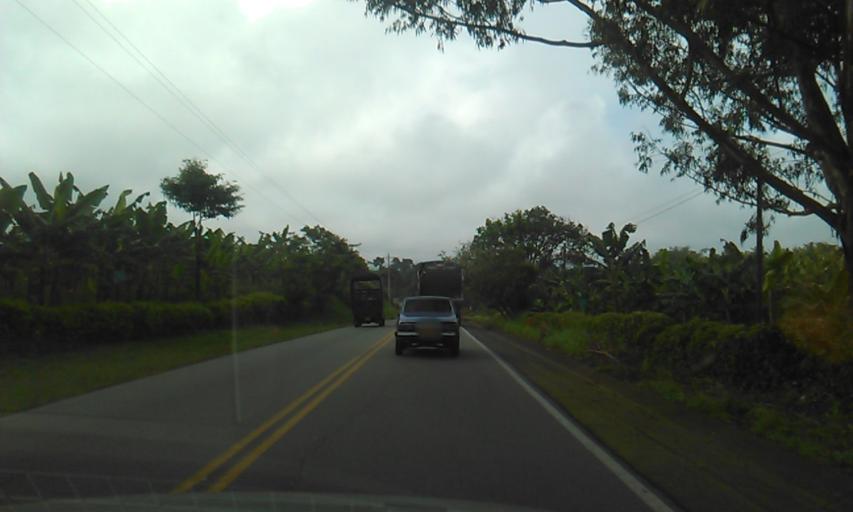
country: CO
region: Quindio
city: Cordoba
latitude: 4.4436
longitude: -75.7178
